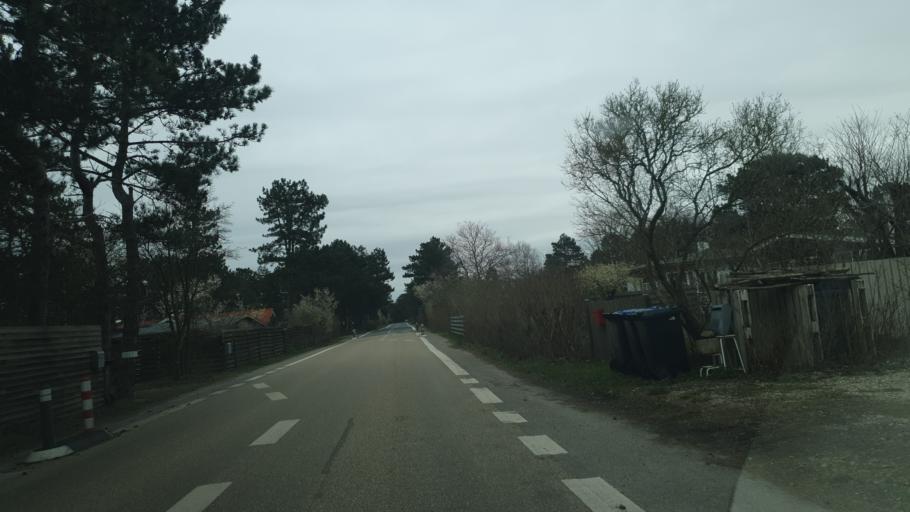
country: DK
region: Zealand
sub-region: Odsherred Kommune
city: Asnaes
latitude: 55.8500
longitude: 11.5085
